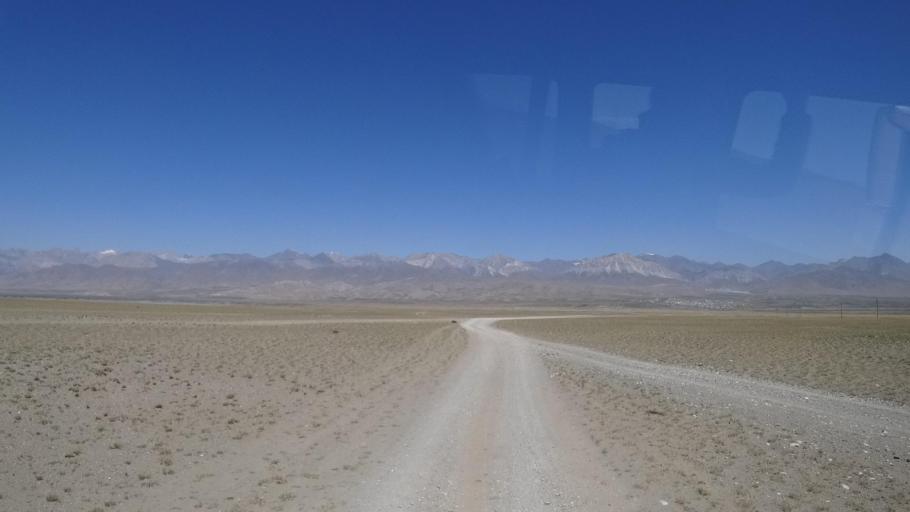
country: KG
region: Osh
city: Gul'cha
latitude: 39.6136
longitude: 72.8745
